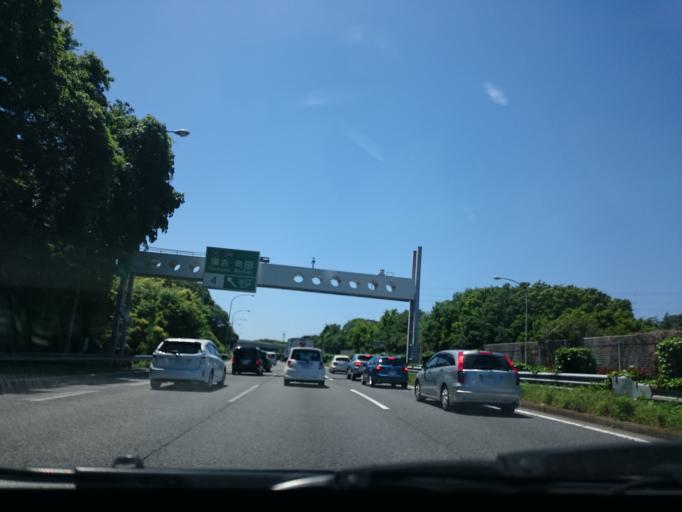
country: JP
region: Tokyo
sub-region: Machida-shi
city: Machida
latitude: 35.5122
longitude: 139.4879
